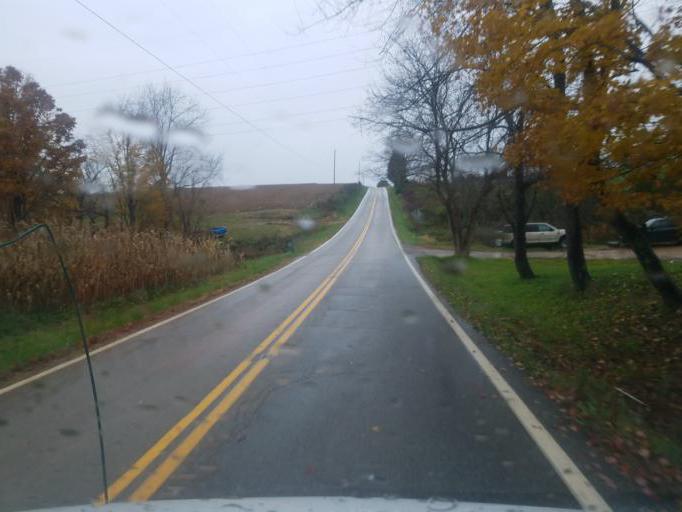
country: US
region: Ohio
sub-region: Washington County
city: Beverly
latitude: 39.4719
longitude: -81.7161
